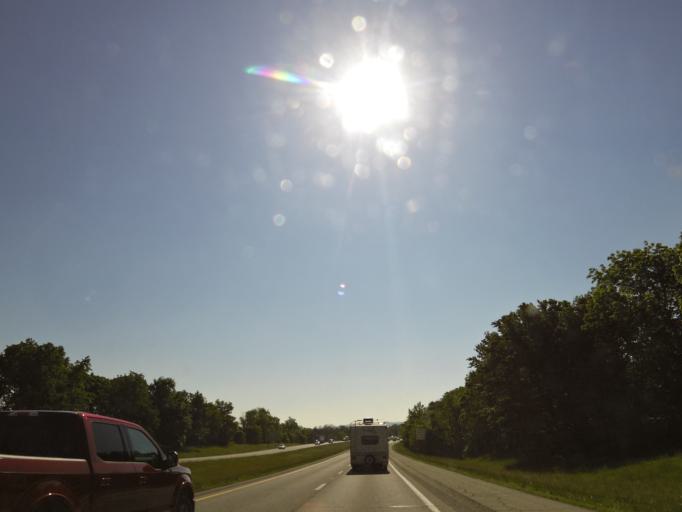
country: US
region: Kentucky
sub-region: Shelby County
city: Shelbyville
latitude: 38.1842
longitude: -85.1969
